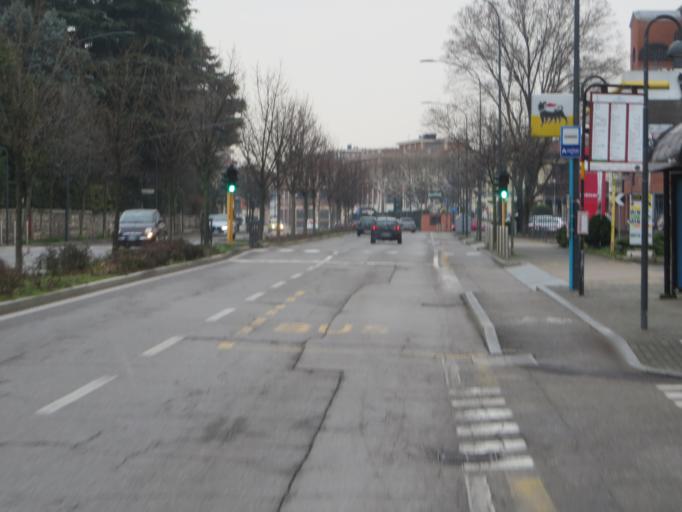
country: IT
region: Lombardy
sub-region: Provincia di Brescia
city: Brescia
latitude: 45.5299
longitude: 10.2530
